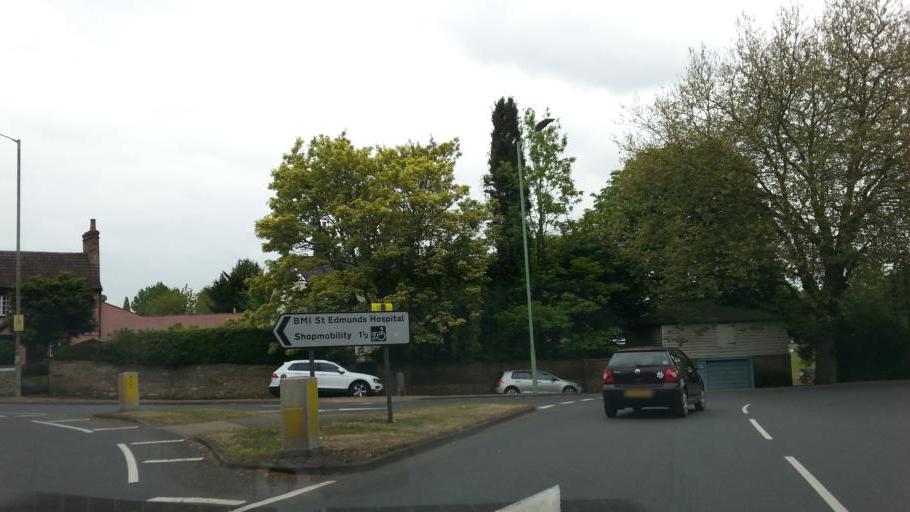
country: GB
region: England
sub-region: Suffolk
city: Bury St Edmunds
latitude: 52.2361
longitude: 0.7249
